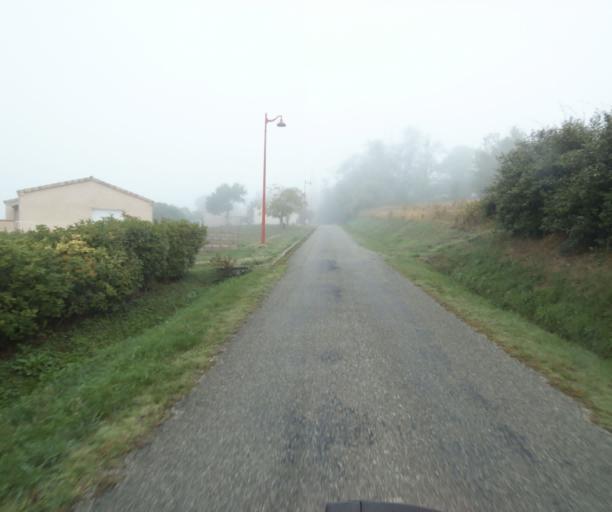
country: FR
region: Midi-Pyrenees
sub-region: Departement du Tarn-et-Garonne
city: Nohic
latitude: 43.9208
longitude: 1.4729
